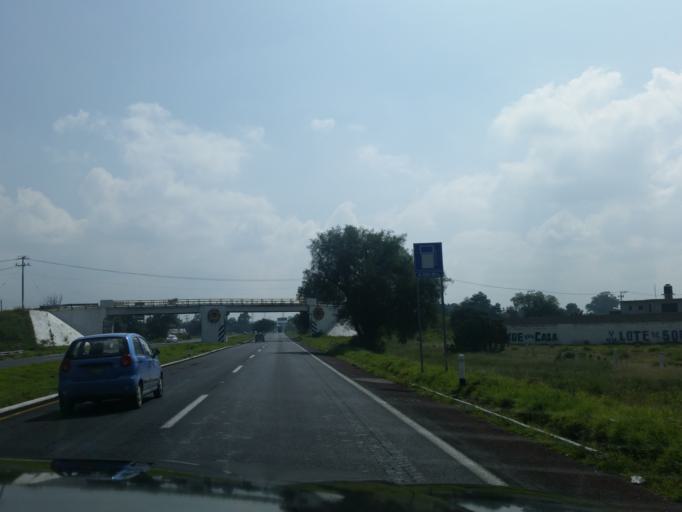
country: MX
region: Morelos
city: Xometla
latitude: 19.6474
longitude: -98.8893
